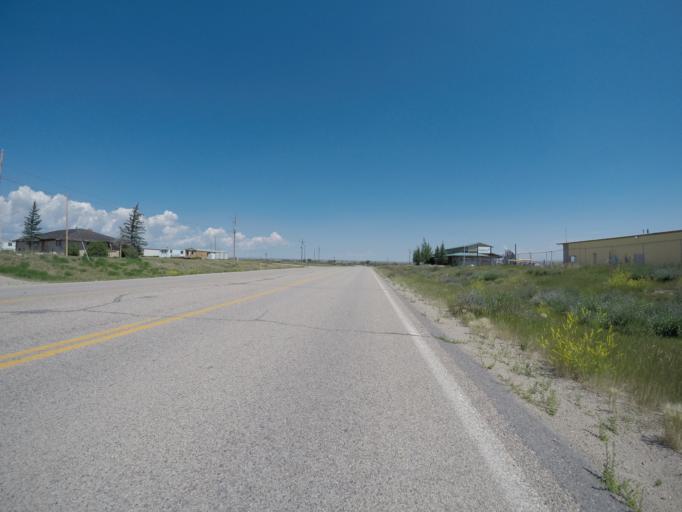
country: US
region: Wyoming
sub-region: Sublette County
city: Marbleton
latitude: 42.5121
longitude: -110.1050
